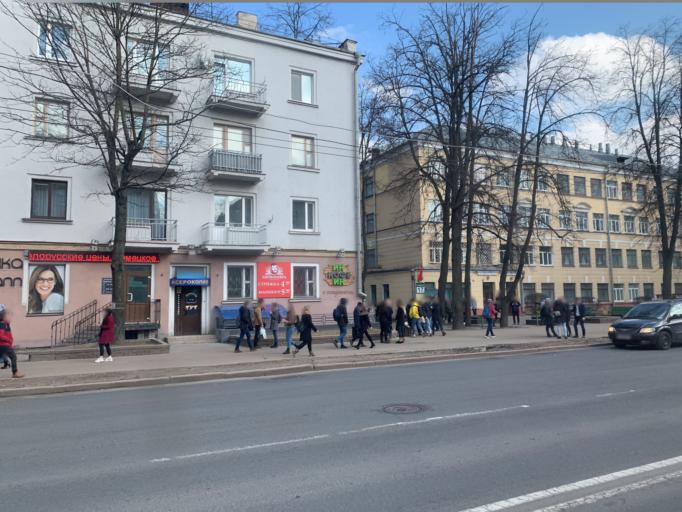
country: BY
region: Minsk
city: Minsk
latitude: 53.8912
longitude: 27.5585
